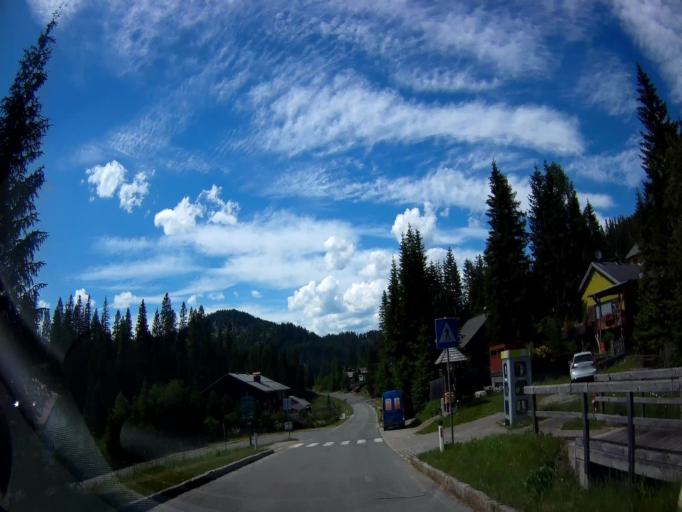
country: AT
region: Carinthia
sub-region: Politischer Bezirk Sankt Veit an der Glan
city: Glodnitz
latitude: 46.9451
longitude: 14.0300
